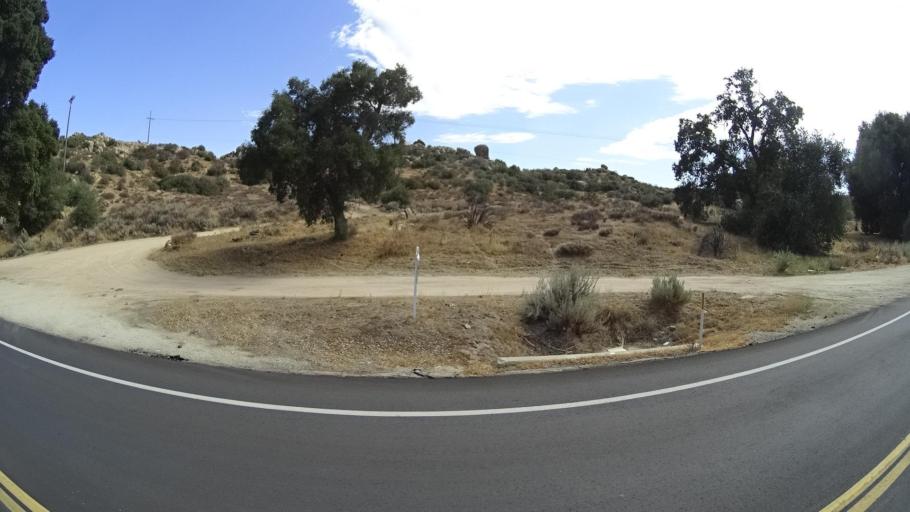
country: MX
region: Baja California
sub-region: Tecate
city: Cereso del Hongo
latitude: 32.6646
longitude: -116.2636
